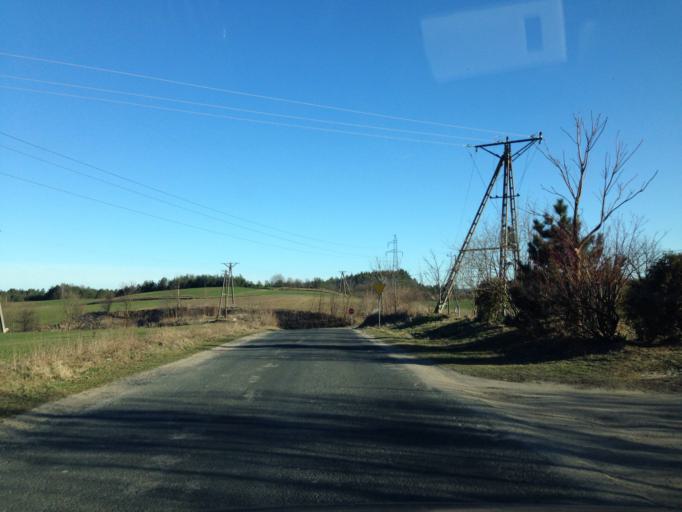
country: PL
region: Warmian-Masurian Voivodeship
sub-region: Powiat nowomiejski
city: Nowe Miasto Lubawskie
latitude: 53.4033
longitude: 19.6087
